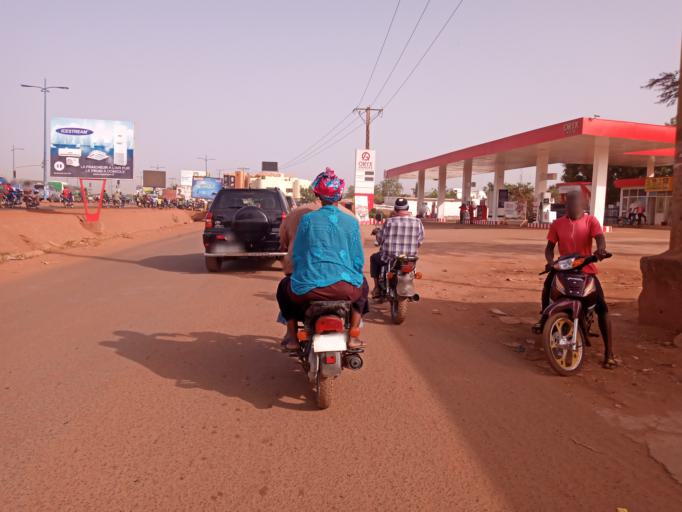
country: ML
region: Bamako
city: Bamako
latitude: 12.6154
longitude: -7.9781
